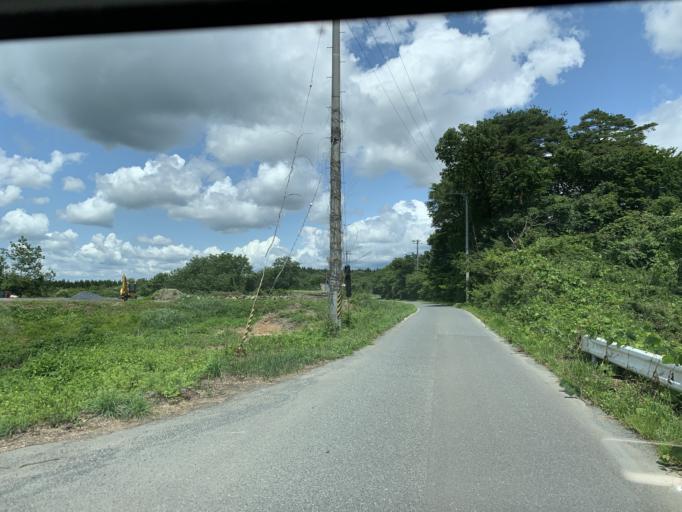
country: JP
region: Iwate
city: Ichinoseki
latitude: 38.9276
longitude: 141.0607
